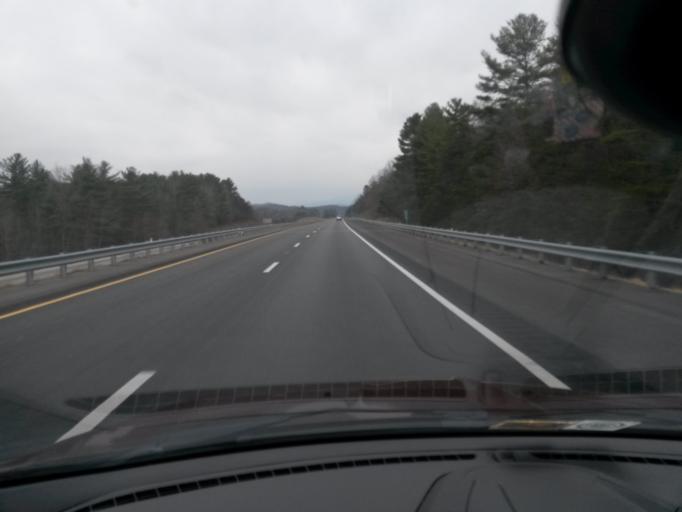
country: US
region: Virginia
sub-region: Alleghany County
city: Clifton Forge
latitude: 37.8082
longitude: -79.6907
